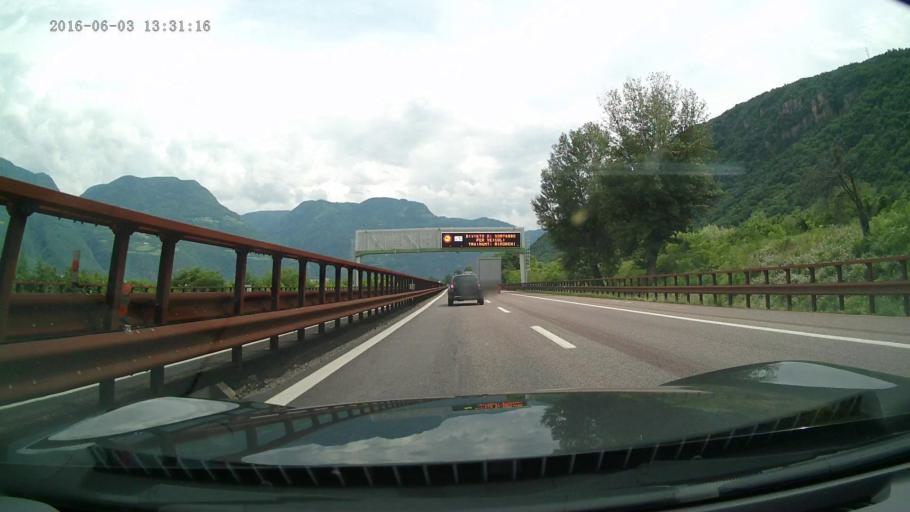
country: IT
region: Trentino-Alto Adige
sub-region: Bolzano
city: Cornaiano
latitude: 46.4534
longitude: 11.3062
